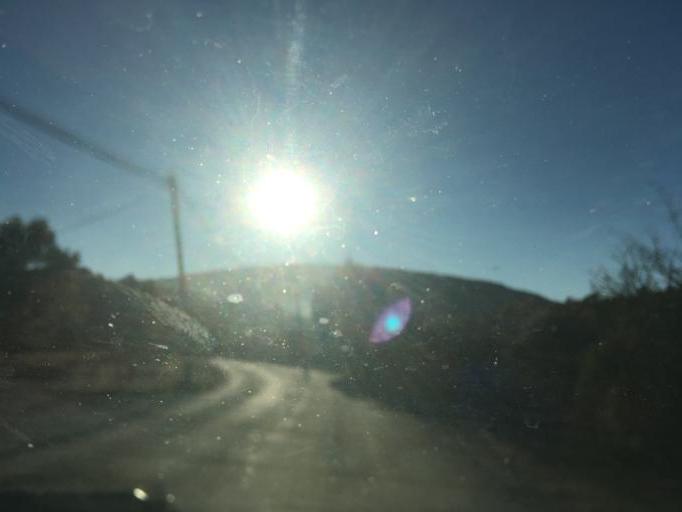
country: FR
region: Provence-Alpes-Cote d'Azur
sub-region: Departement du Var
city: Flayosc
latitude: 43.6046
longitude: 6.3672
